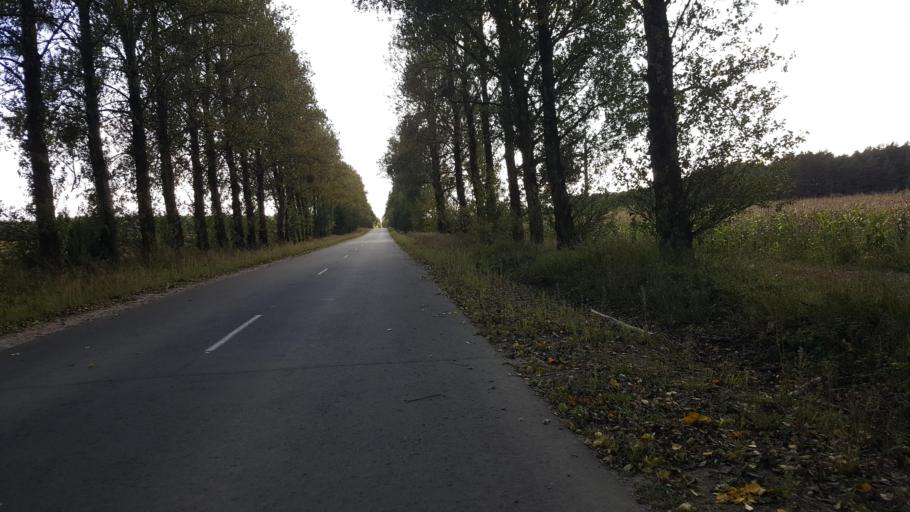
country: BY
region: Brest
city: Kamyanyets
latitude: 52.4104
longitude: 23.9152
